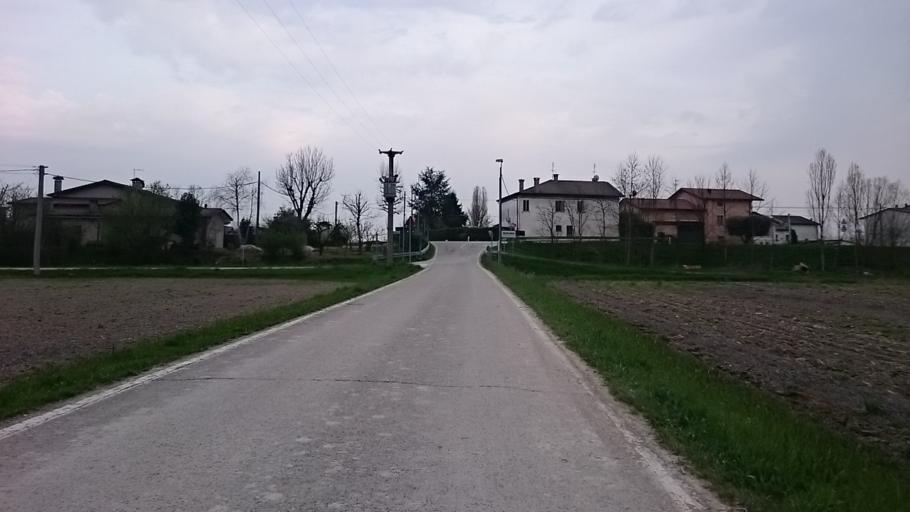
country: IT
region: Veneto
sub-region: Provincia di Padova
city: Tremignon
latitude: 45.5245
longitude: 11.8099
